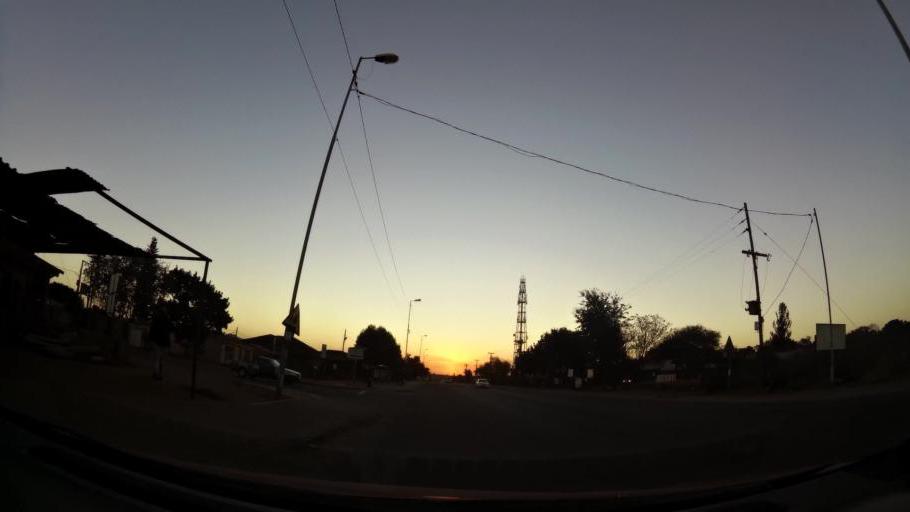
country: ZA
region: North-West
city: Ga-Rankuwa
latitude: -25.6050
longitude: 27.9980
